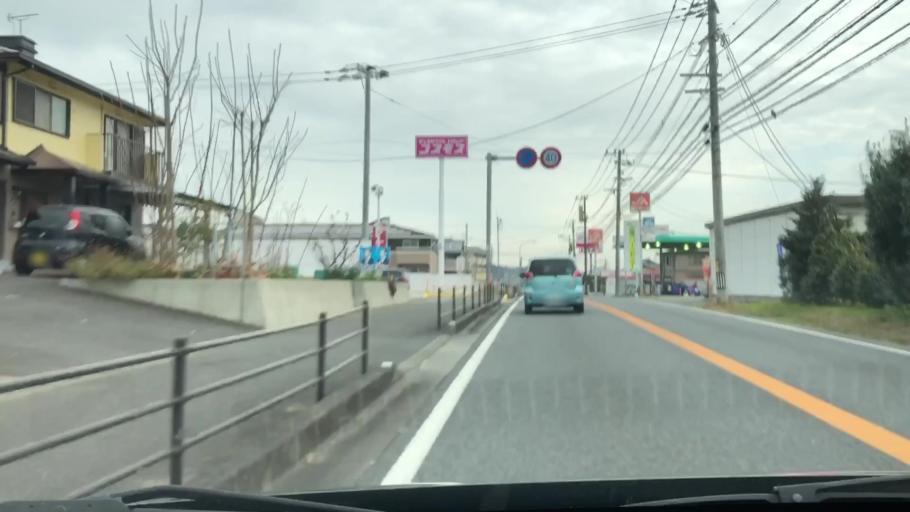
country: JP
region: Oita
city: Takedamachi
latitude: 32.9933
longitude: 131.6135
